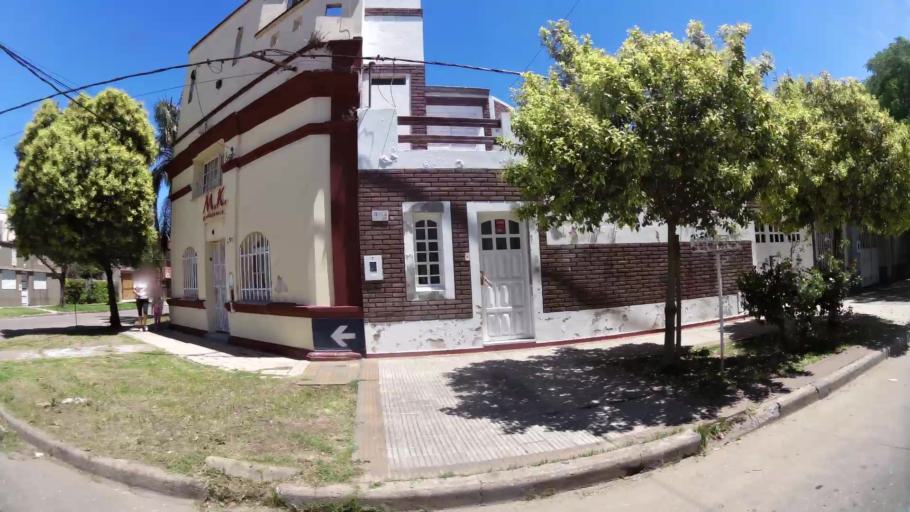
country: AR
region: Santa Fe
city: Santa Fe de la Vera Cruz
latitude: -31.6286
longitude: -60.7082
